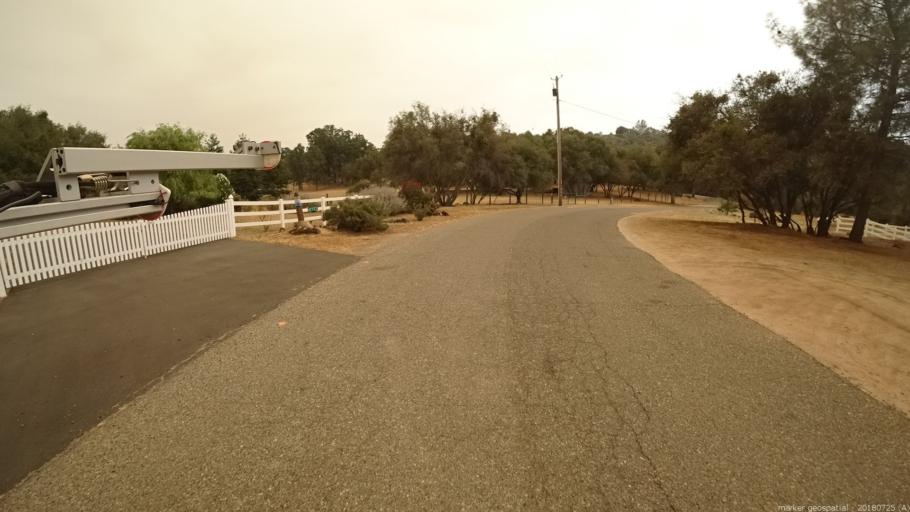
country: US
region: California
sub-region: Madera County
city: Coarsegold
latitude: 37.1999
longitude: -119.6761
